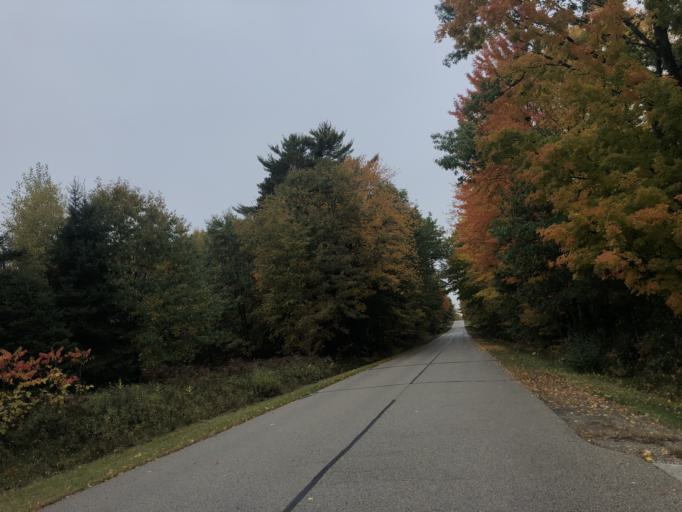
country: US
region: Wisconsin
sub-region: Oconto County
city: Oconto Falls
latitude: 44.8731
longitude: -88.0271
